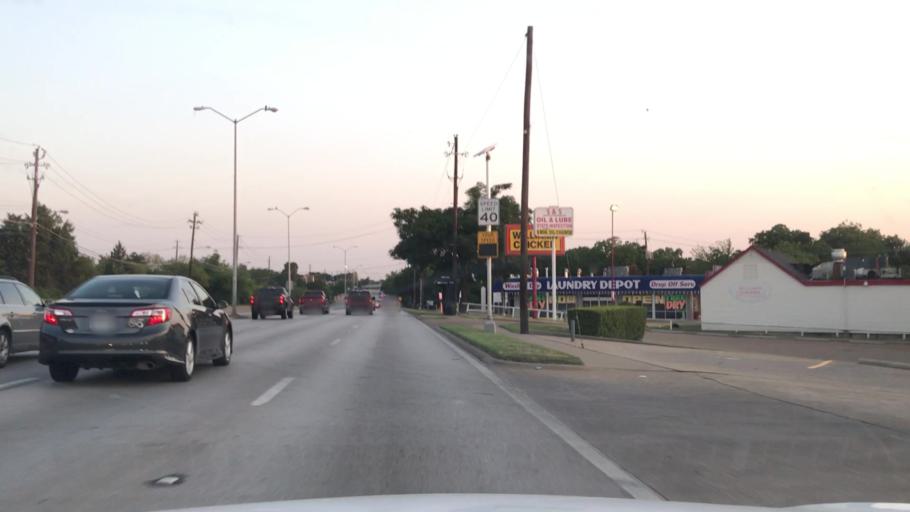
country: US
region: Texas
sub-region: Dallas County
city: Mesquite
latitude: 32.8107
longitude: -96.6847
